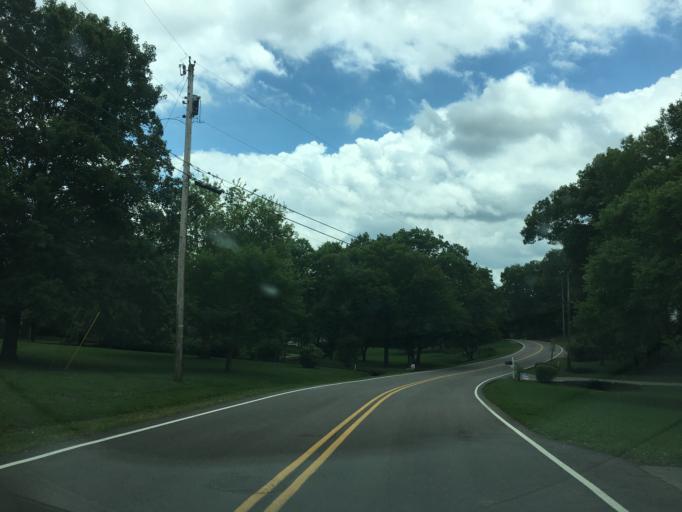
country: US
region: Tennessee
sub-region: Davidson County
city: Belle Meade
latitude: 36.0868
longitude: -86.8412
